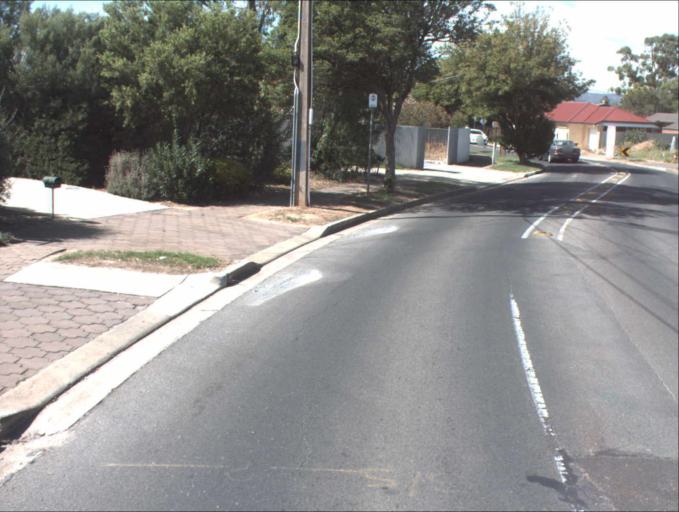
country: AU
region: South Australia
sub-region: Port Adelaide Enfield
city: Klemzig
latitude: -34.8744
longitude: 138.6386
